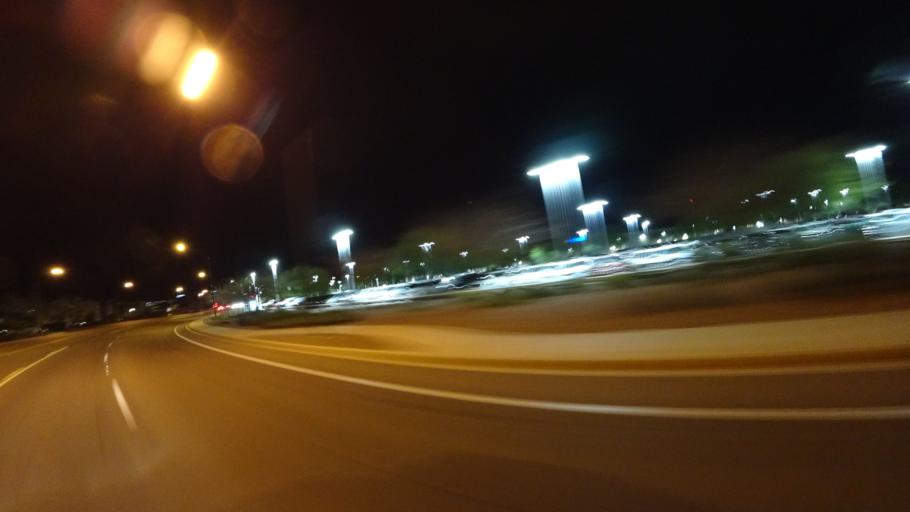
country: US
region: Arizona
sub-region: Maricopa County
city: Gilbert
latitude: 33.2951
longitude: -111.7587
